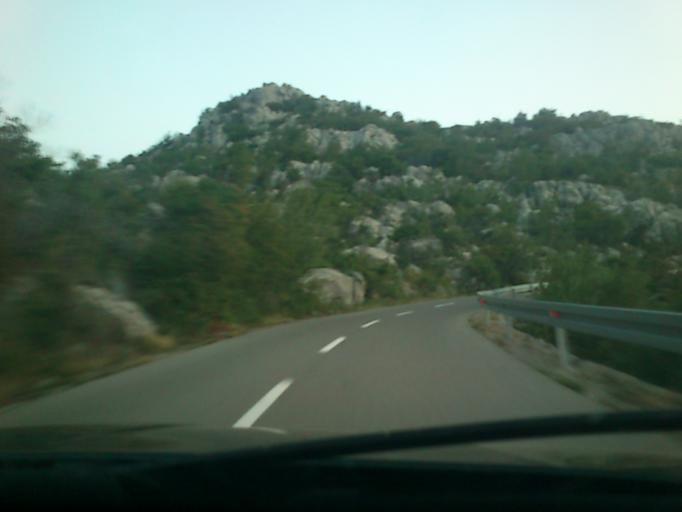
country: HR
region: Licko-Senjska
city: Senj
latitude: 44.9205
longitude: 14.9234
